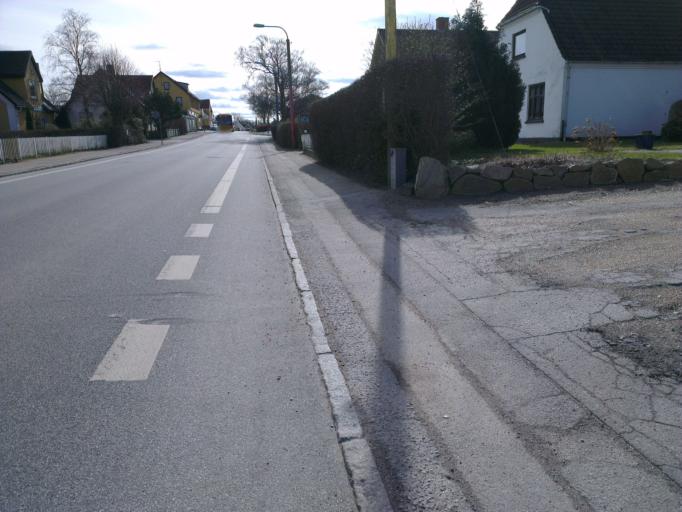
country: DK
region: Capital Region
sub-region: Frederikssund Kommune
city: Skibby
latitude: 55.7533
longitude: 11.9592
